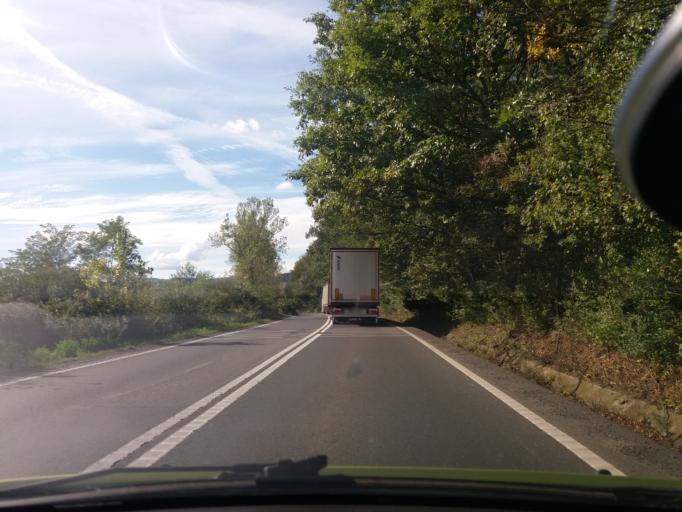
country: RO
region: Arad
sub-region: Comuna Petris
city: Petris
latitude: 46.0108
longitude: 22.3737
